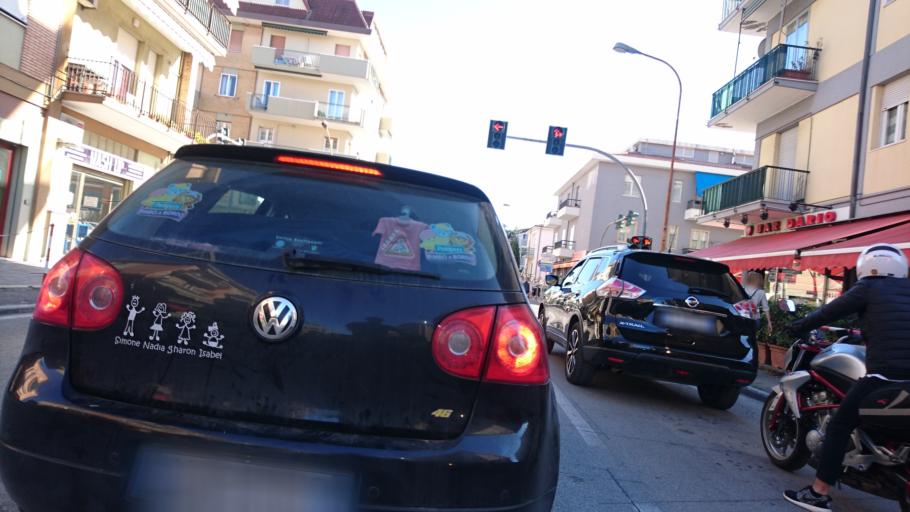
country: IT
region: The Marches
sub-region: Provincia di Pesaro e Urbino
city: Pesaro
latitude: 43.8967
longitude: 12.9068
